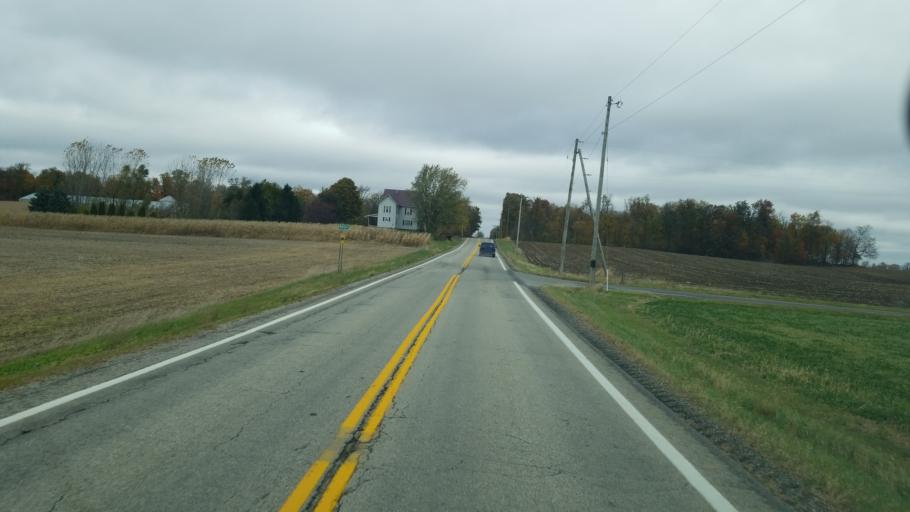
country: US
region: Ohio
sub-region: Crawford County
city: Bucyrus
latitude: 40.8573
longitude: -82.8556
